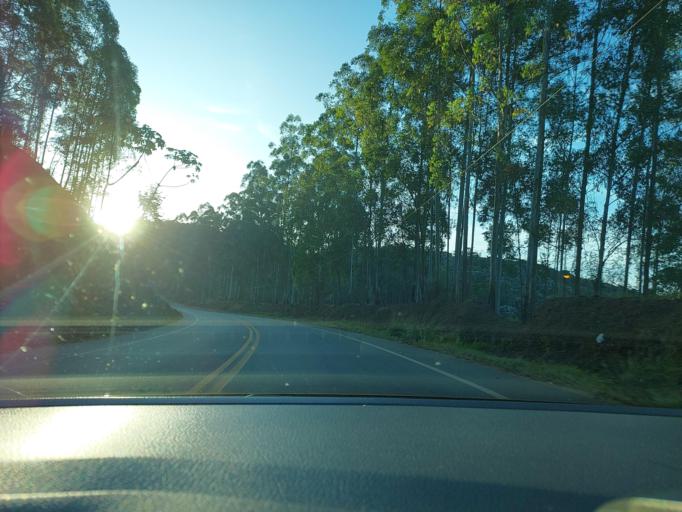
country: BR
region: Minas Gerais
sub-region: Vicosa
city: Vicosa
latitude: -20.8283
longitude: -42.8150
